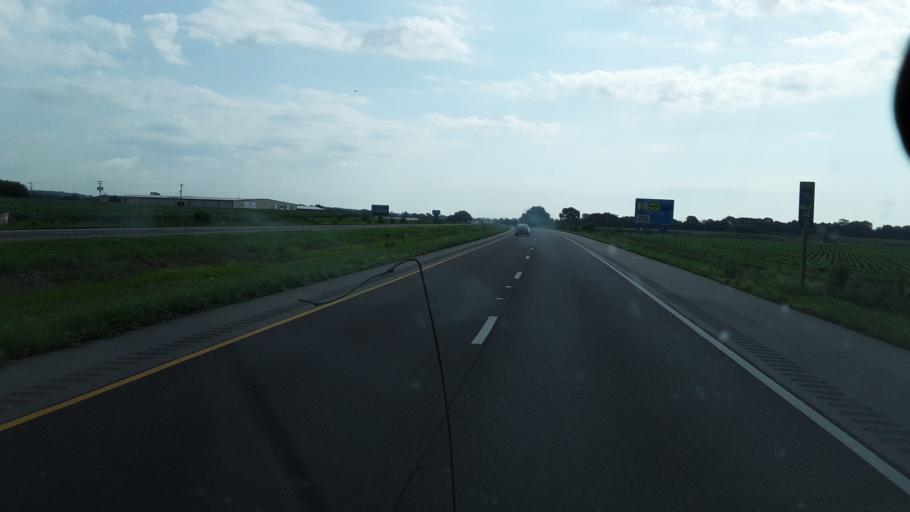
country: US
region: Illinois
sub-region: Bond County
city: Greenville
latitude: 38.8629
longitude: -89.4049
